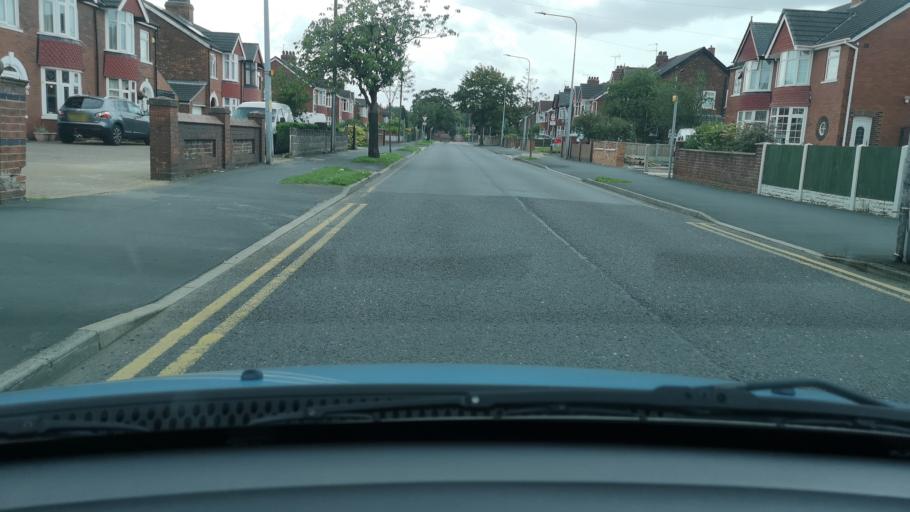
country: GB
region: England
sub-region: North Lincolnshire
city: Scunthorpe
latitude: 53.5895
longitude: -0.6610
